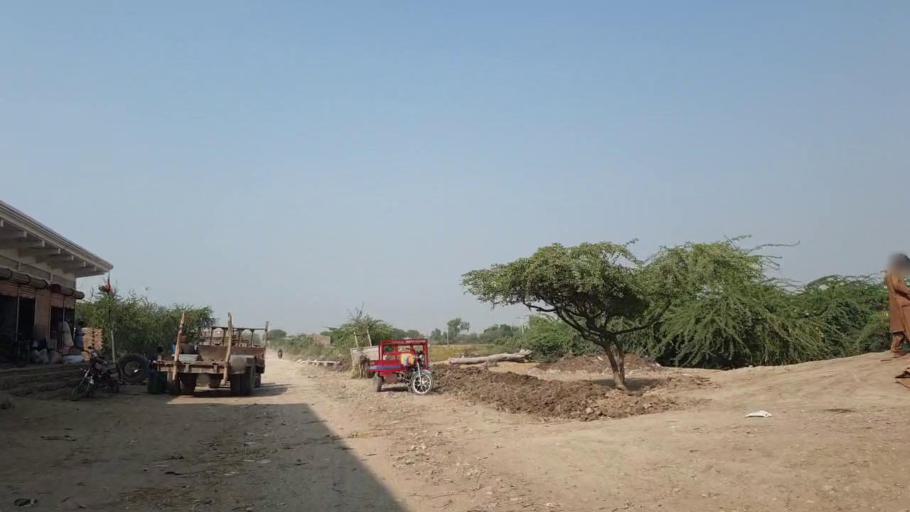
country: PK
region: Sindh
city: Kario
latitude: 24.9286
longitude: 68.5604
